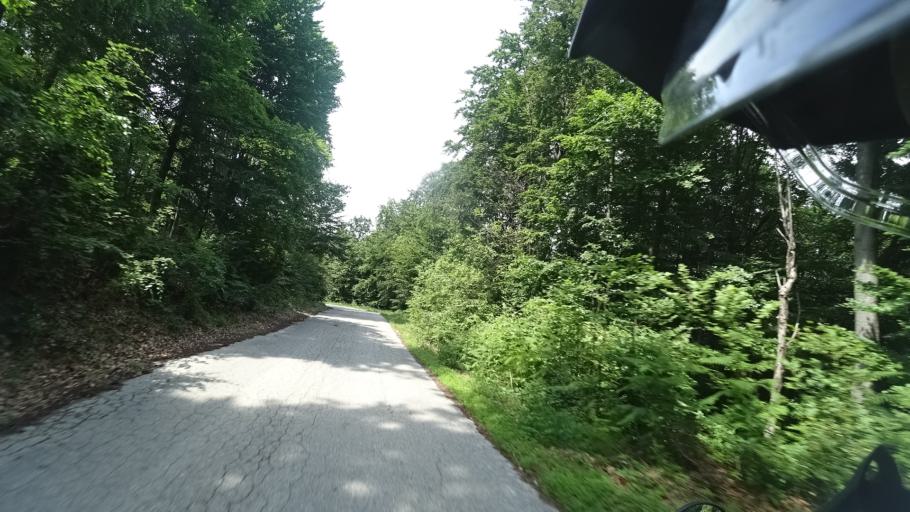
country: HR
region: Sisacko-Moslavacka
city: Gvozd
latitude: 45.3080
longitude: 15.8020
